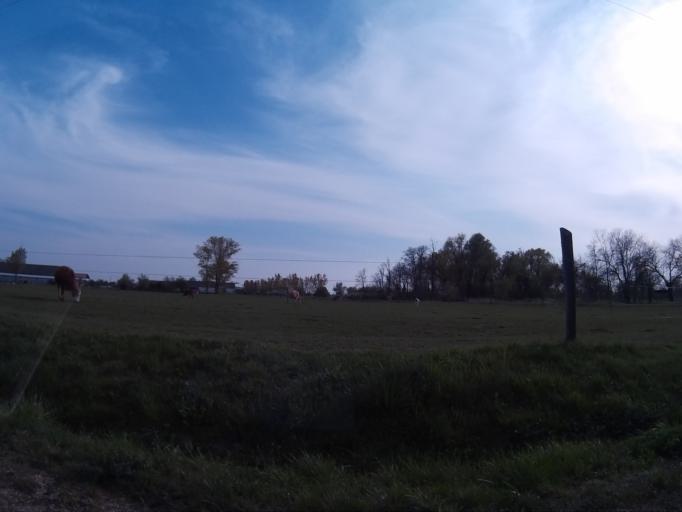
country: HU
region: Vas
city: Celldomolk
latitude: 47.1882
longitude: 17.0914
